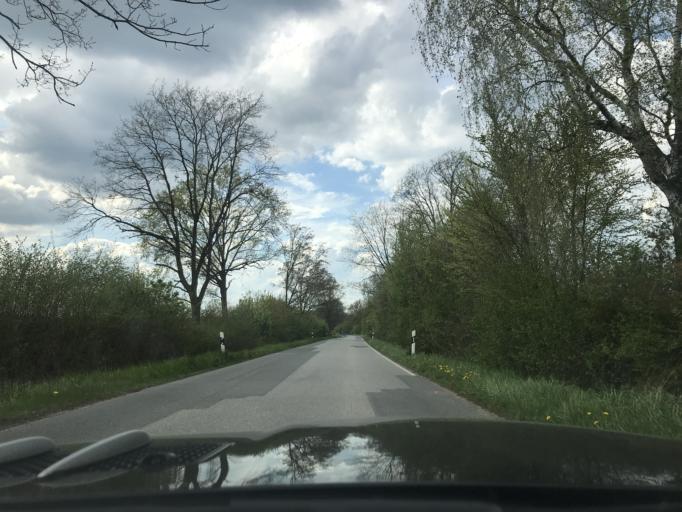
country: DE
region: Schleswig-Holstein
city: Timmendorfer Strand
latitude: 53.9588
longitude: 10.7979
